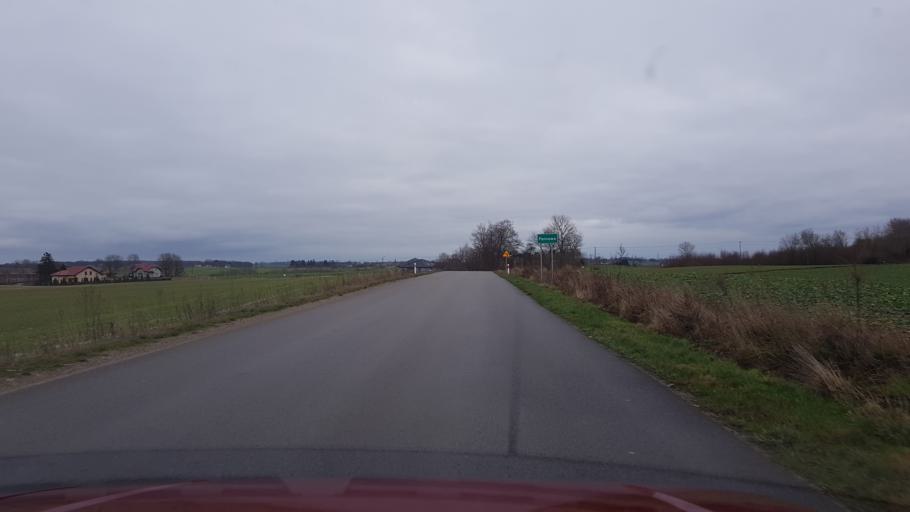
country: PL
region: West Pomeranian Voivodeship
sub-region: Powiat koszalinski
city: Mielno
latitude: 54.1701
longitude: 16.0099
